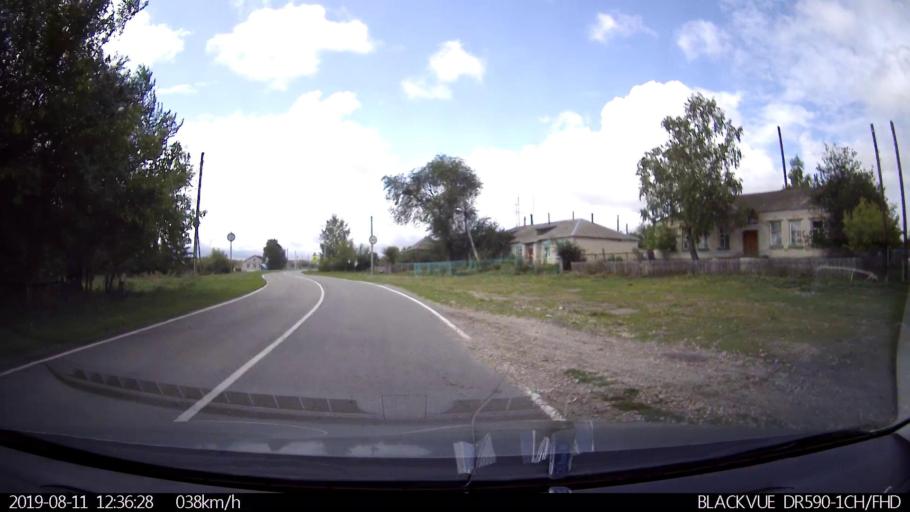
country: RU
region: Ulyanovsk
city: Ignatovka
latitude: 53.8246
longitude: 47.8219
